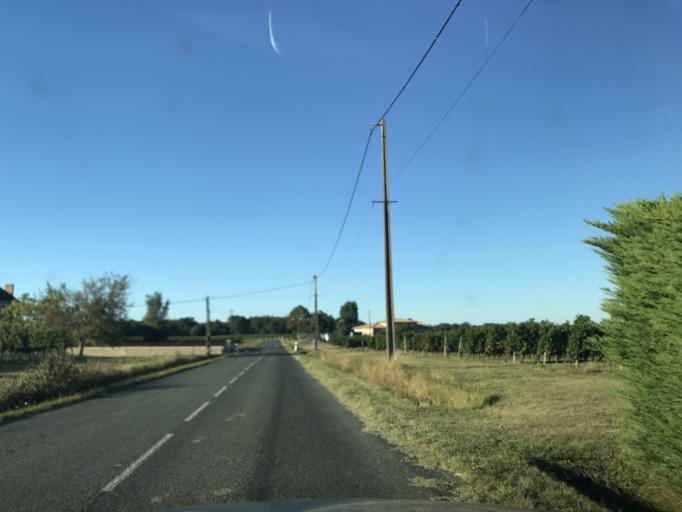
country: FR
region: Aquitaine
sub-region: Departement de la Gironde
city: Sauveterre-de-Guyenne
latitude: 44.7186
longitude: -0.0649
